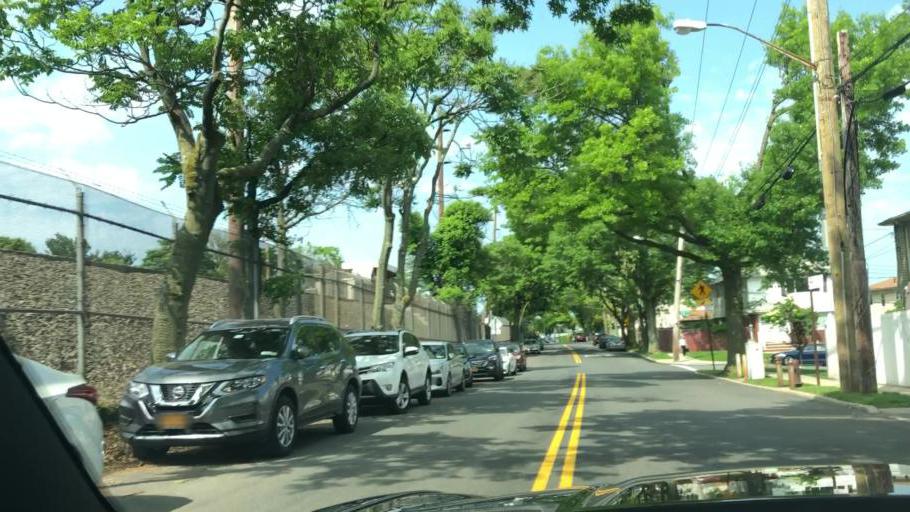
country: US
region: New York
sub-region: Richmond County
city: Staten Island
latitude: 40.5556
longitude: -74.1378
